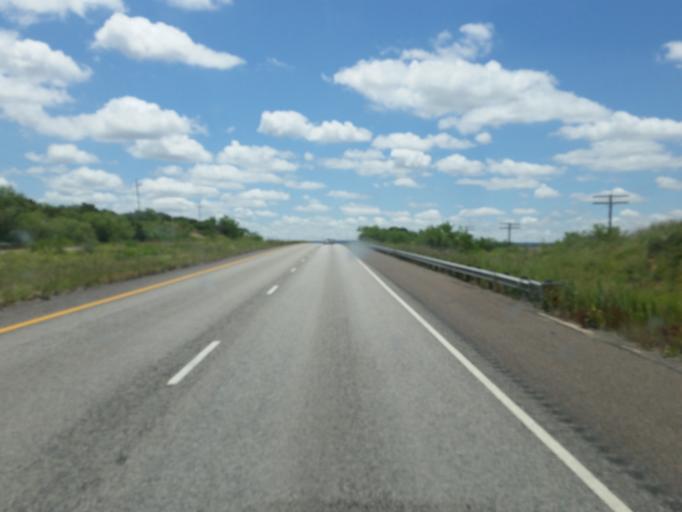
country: US
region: Texas
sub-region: Garza County
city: Post
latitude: 33.0235
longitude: -101.1829
